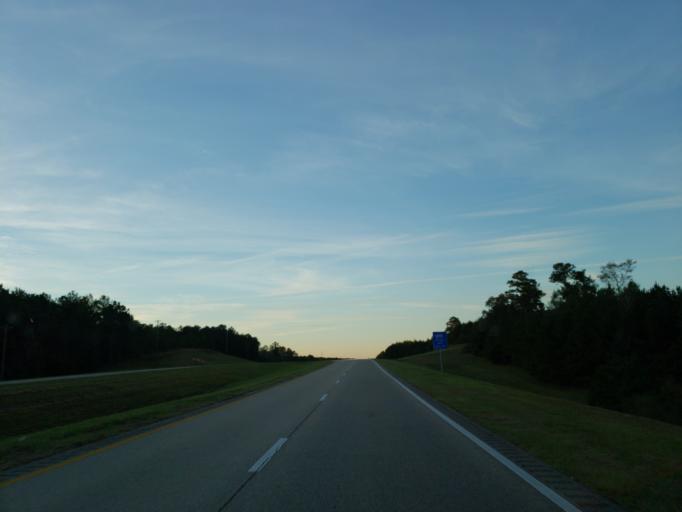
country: US
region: Mississippi
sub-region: Wayne County
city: Belmont
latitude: 31.4795
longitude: -88.4831
